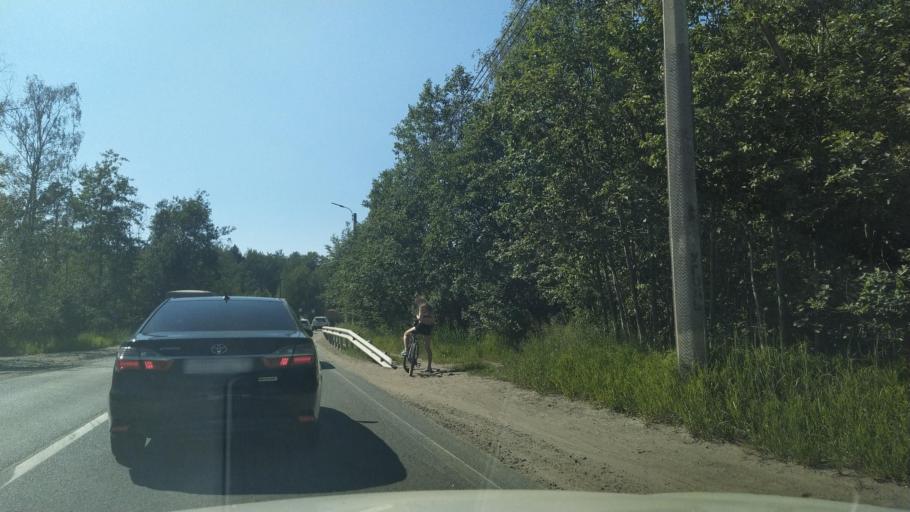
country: RU
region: St.-Petersburg
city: Beloostrov
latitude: 60.1419
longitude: 30.0204
